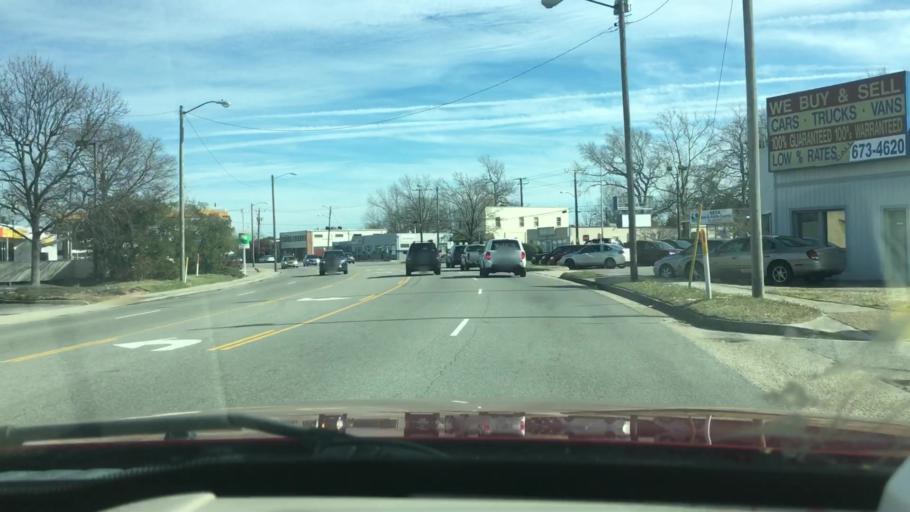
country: US
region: Virginia
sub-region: City of Portsmouth
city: Portsmouth Heights
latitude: 36.8348
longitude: -76.3461
